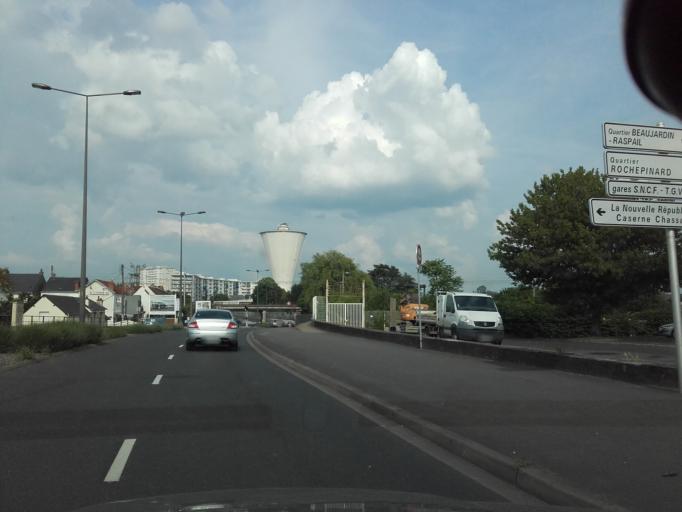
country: FR
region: Centre
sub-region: Departement d'Indre-et-Loire
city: Tours
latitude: 47.3743
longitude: 0.7014
